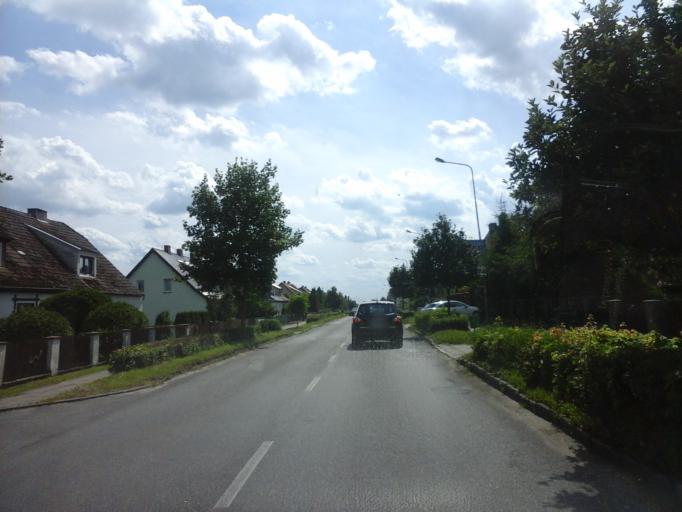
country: PL
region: West Pomeranian Voivodeship
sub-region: Powiat swidwinski
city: Swidwin
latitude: 53.7699
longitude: 15.7610
